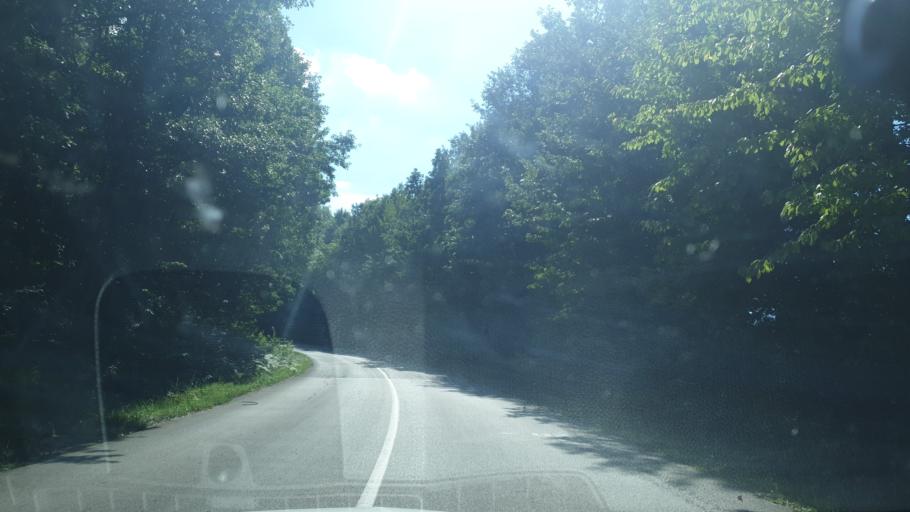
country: RS
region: Central Serbia
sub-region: Zlatiborski Okrug
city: Kosjeric
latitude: 44.0347
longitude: 20.0154
